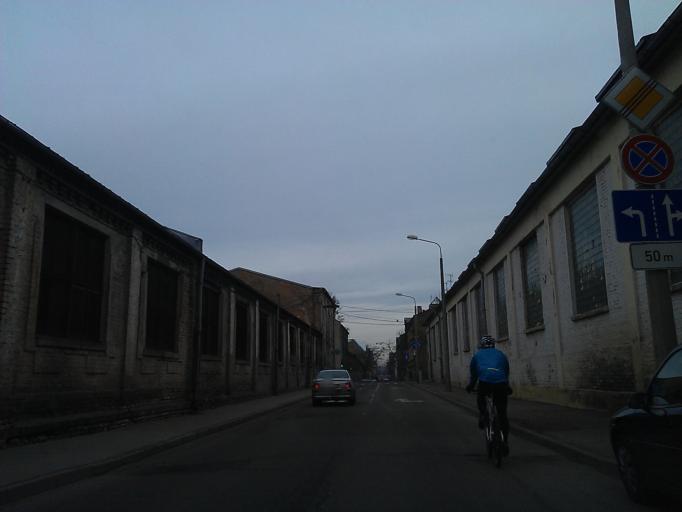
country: LV
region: Riga
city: Riga
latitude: 56.9485
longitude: 24.1468
